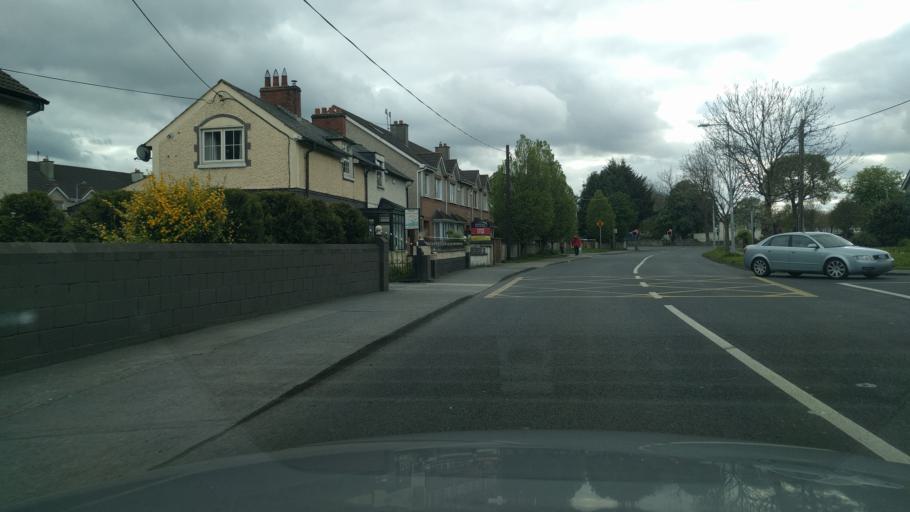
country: IE
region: Leinster
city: Clondalkin
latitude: 53.3309
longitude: -6.3962
